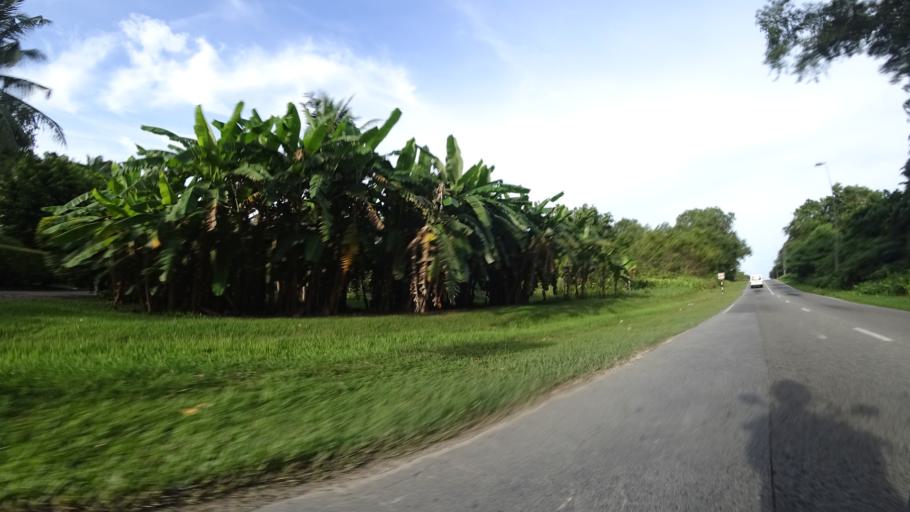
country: BN
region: Brunei and Muara
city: Bandar Seri Begawan
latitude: 4.8716
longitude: 114.8181
